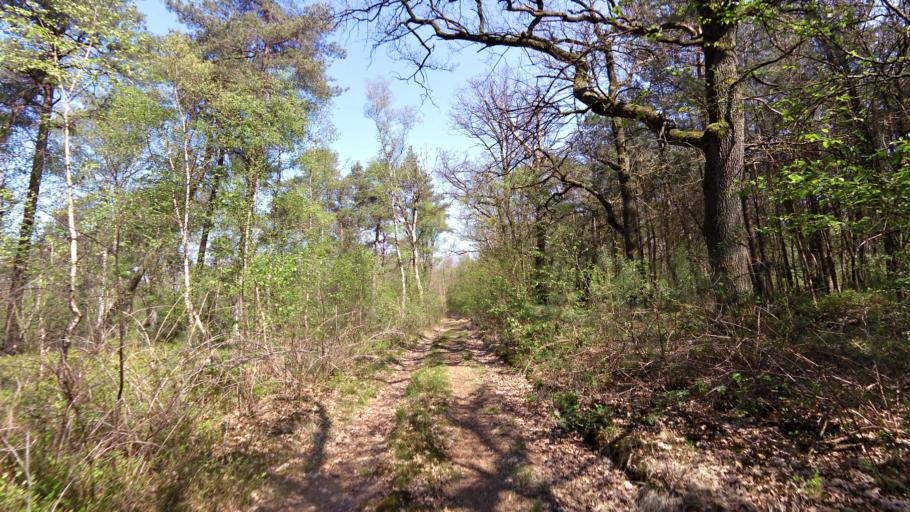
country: NL
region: Gelderland
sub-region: Gemeente Renkum
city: Wolfheze
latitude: 52.0220
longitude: 5.8126
